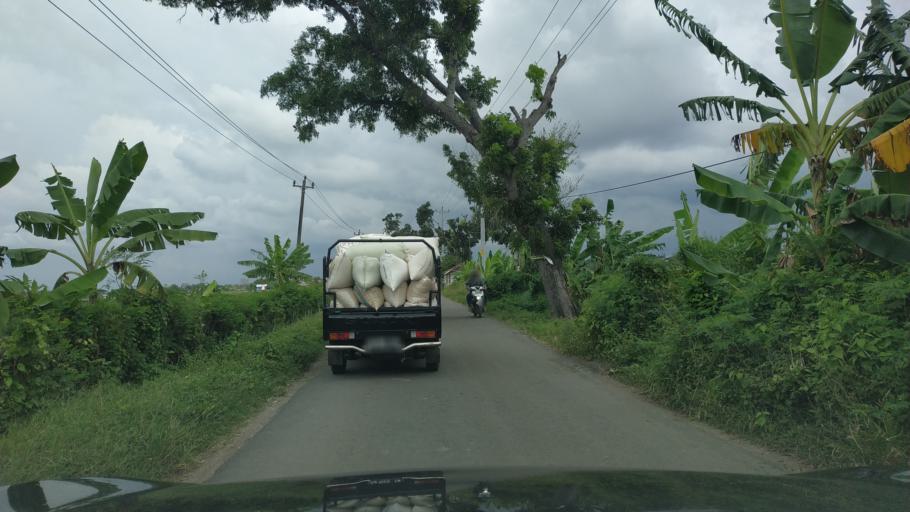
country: ID
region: Central Java
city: Pemalang
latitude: -6.9225
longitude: 109.3345
